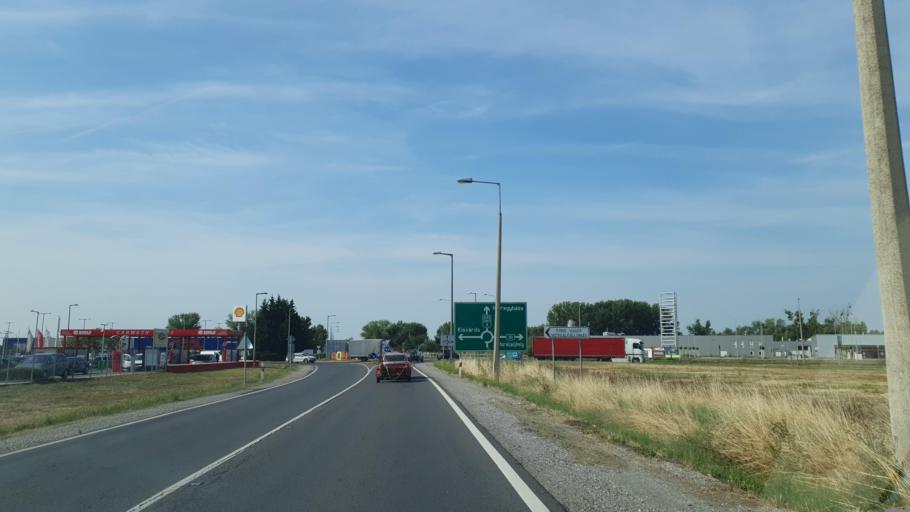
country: HU
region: Szabolcs-Szatmar-Bereg
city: Kisvarda
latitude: 48.2345
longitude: 22.0644
